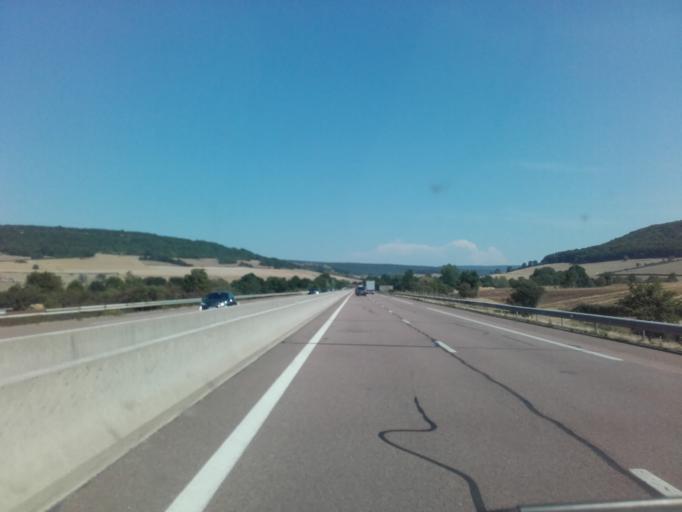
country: FR
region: Bourgogne
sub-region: Departement de la Cote-d'Or
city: Pouilly-en-Auxois
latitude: 47.2067
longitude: 4.6296
